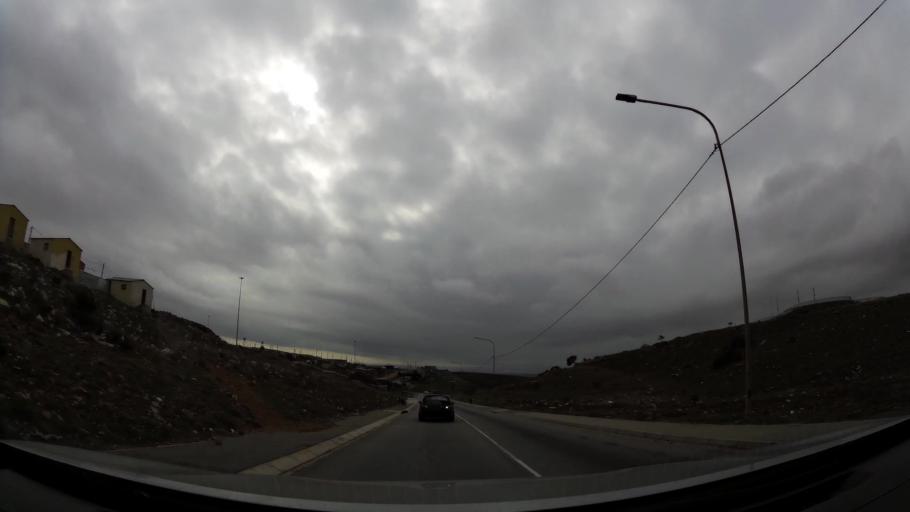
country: ZA
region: Eastern Cape
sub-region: Nelson Mandela Bay Metropolitan Municipality
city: Port Elizabeth
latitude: -33.9129
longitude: 25.5377
